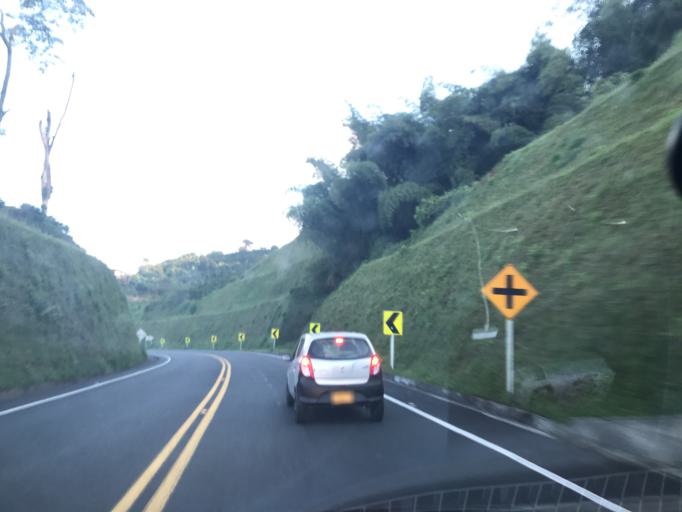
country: CO
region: Risaralda
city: Pereira
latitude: 4.7769
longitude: -75.7142
